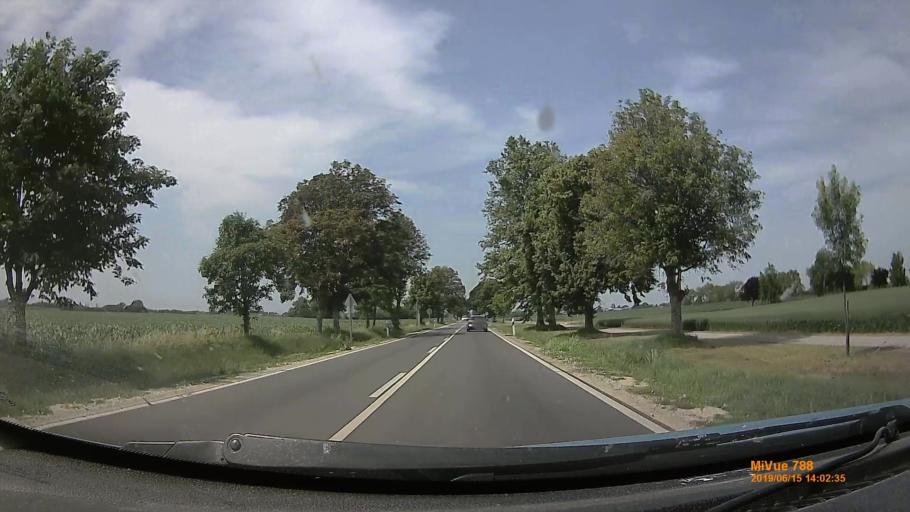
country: HU
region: Somogy
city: Siofok
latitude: 46.8612
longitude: 18.0864
